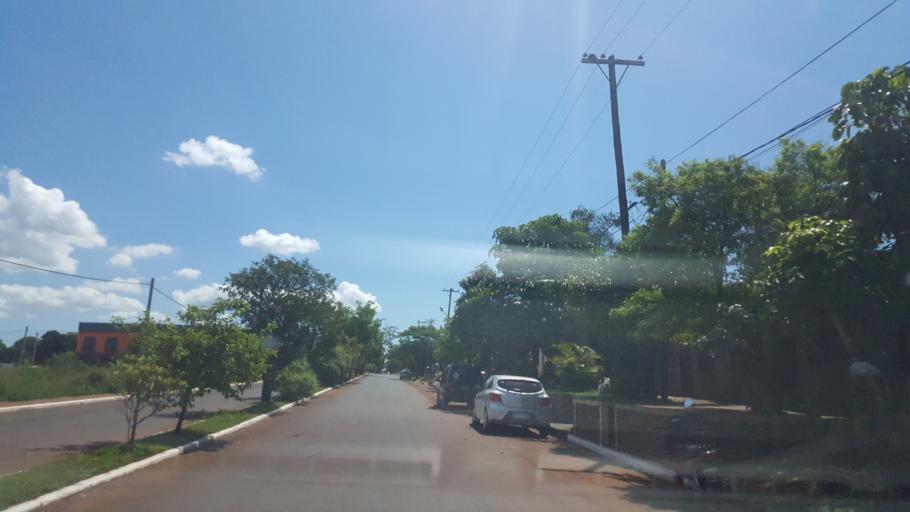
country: AR
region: Misiones
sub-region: Departamento de Capital
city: Posadas
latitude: -27.3816
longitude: -55.9241
